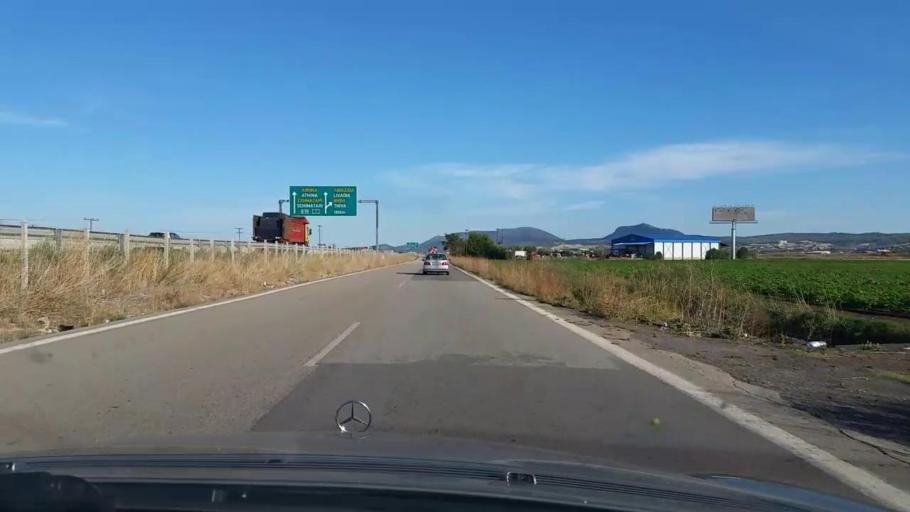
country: GR
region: Central Greece
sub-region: Nomos Voiotias
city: Thivai
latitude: 38.3661
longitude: 23.3064
